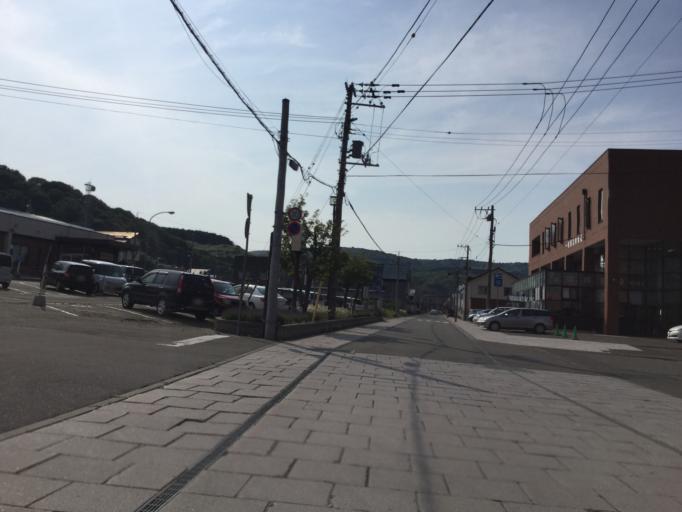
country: JP
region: Hokkaido
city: Wakkanai
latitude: 45.3983
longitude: 141.6838
